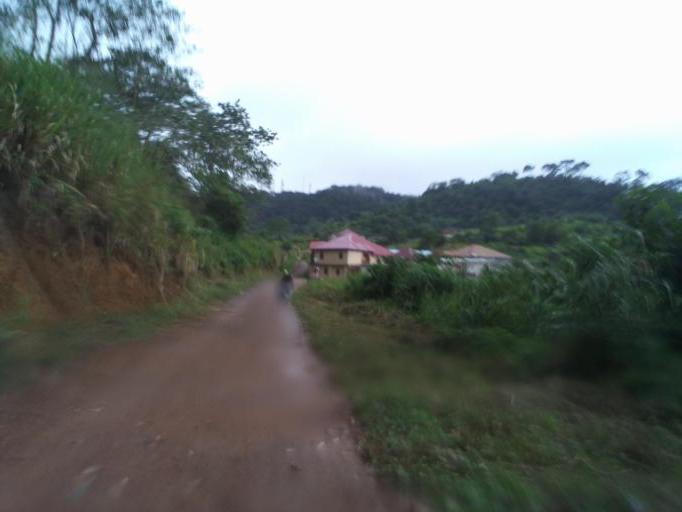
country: SL
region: Eastern Province
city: Kenema
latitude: 7.8555
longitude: -11.2079
